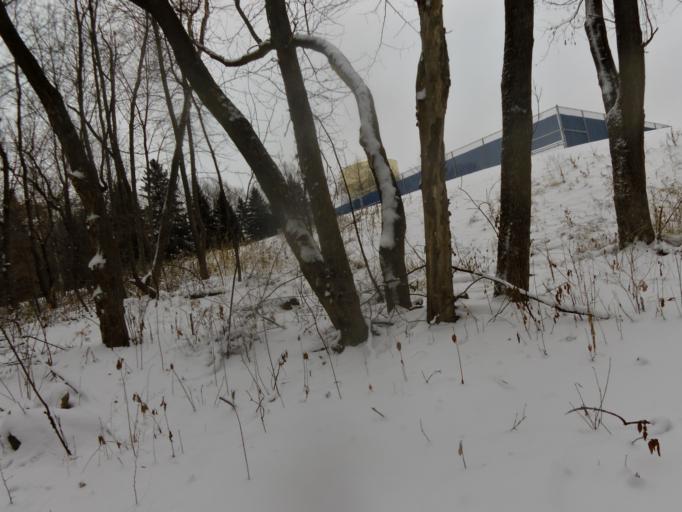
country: US
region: Minnesota
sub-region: Dakota County
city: Inver Grove Heights
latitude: 44.8668
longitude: -93.0737
